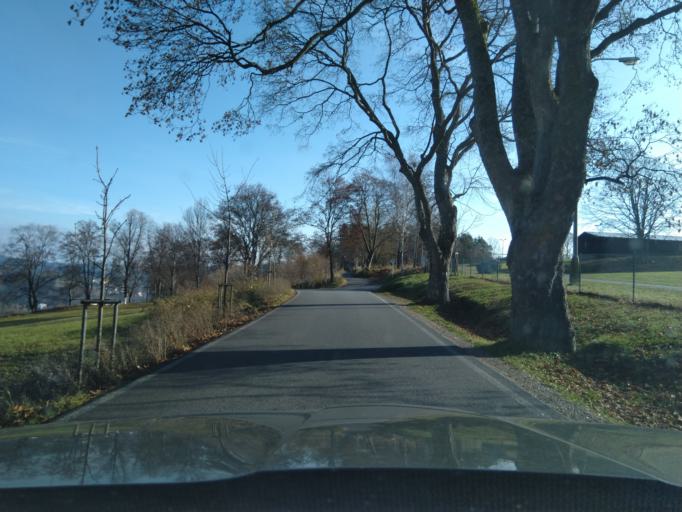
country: CZ
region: Jihocesky
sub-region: Okres Prachatice
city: Vimperk
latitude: 49.0598
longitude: 13.7630
